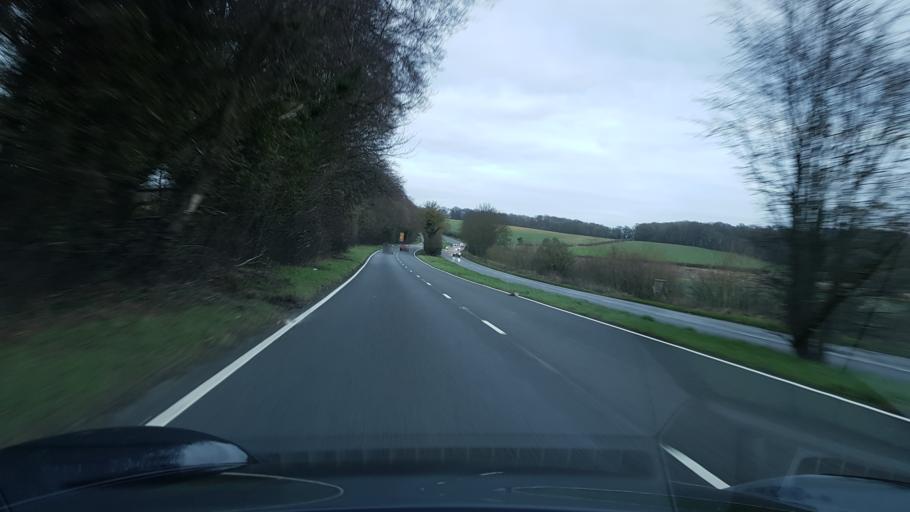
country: GB
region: England
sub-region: Hampshire
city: Kings Worthy
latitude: 51.0686
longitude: -1.2115
